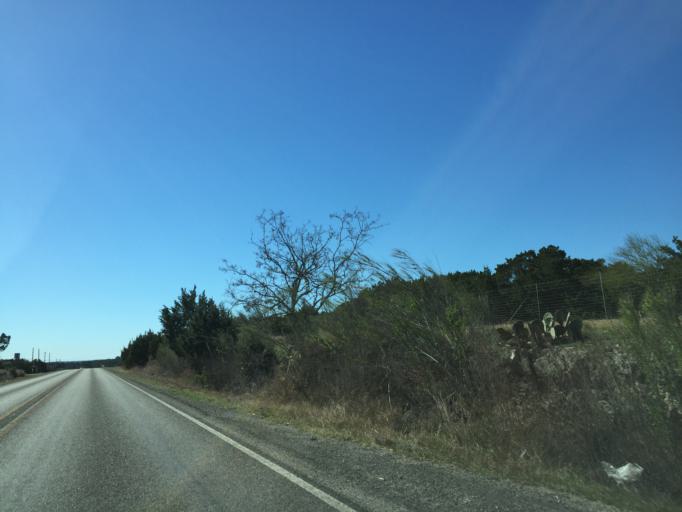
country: US
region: Texas
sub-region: Comal County
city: Garden Ridge
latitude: 29.7474
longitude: -98.3036
